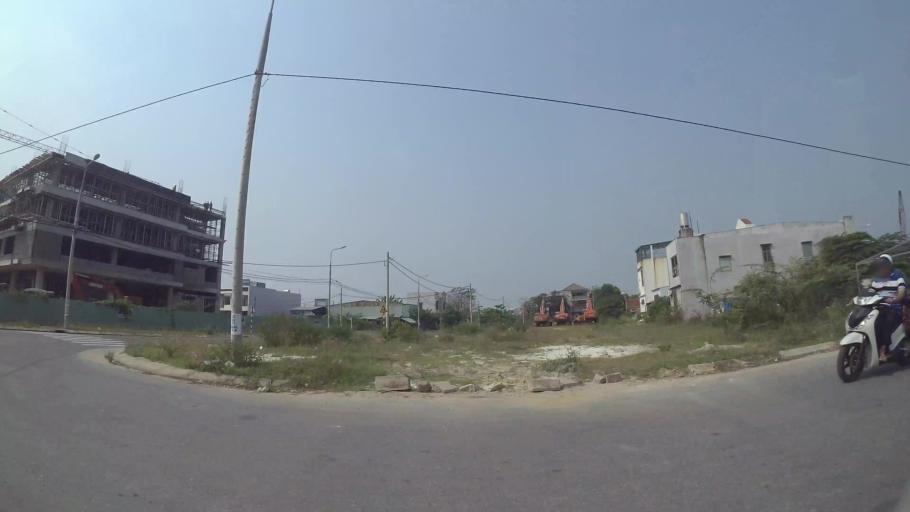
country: VN
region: Da Nang
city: Cam Le
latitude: 16.0042
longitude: 108.2206
